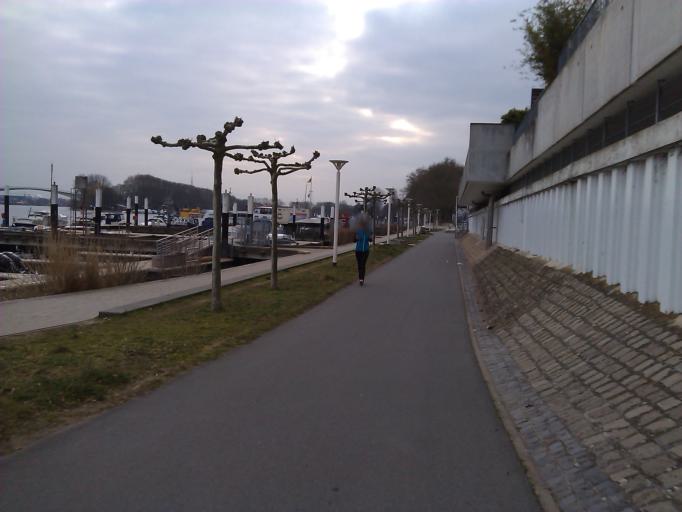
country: DE
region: Rheinland-Pfalz
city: Budenheim
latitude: 50.0422
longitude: 8.2025
